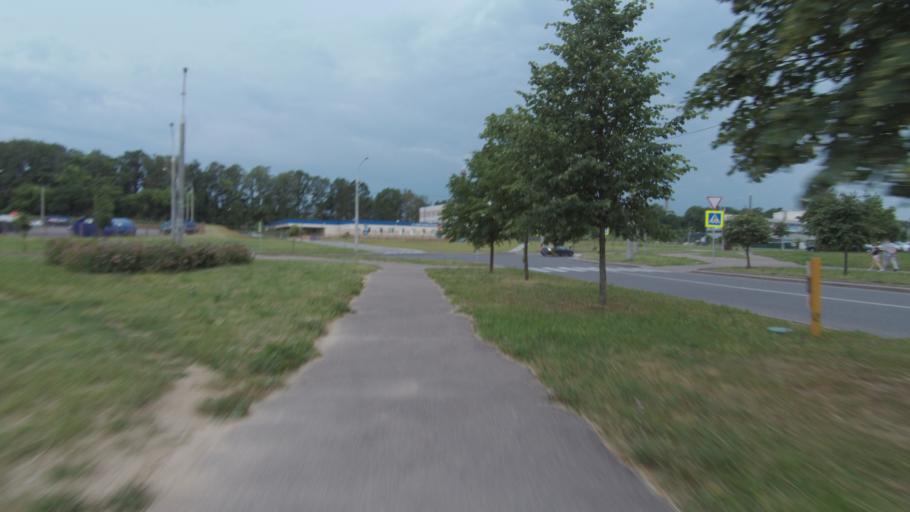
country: BY
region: Minsk
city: Syenitsa
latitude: 53.8407
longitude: 27.5628
